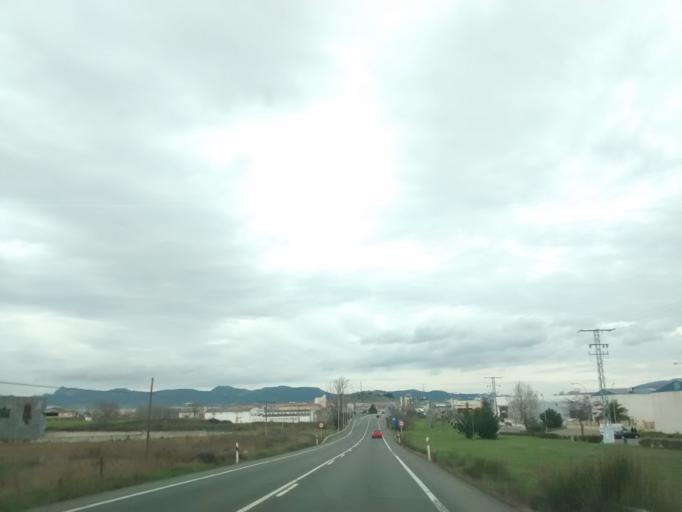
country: ES
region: La Rioja
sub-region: Provincia de La Rioja
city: Ollauri
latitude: 42.5578
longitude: -2.8363
